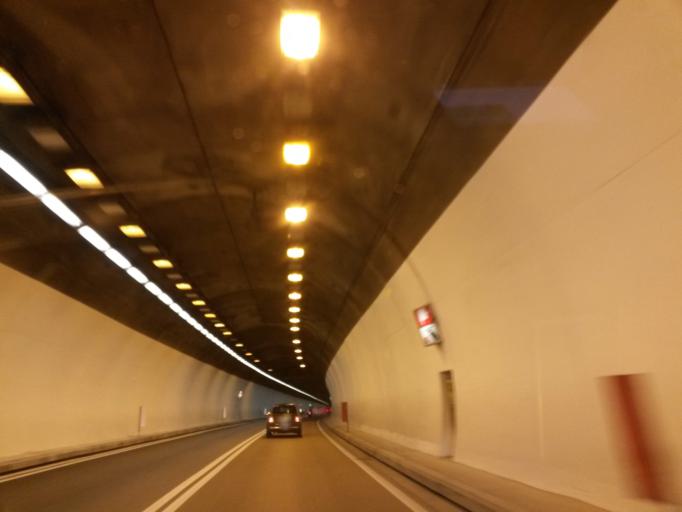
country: IT
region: Trentino-Alto Adige
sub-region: Provincia di Trento
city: Riva del Garda
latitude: 45.8792
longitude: 10.8376
